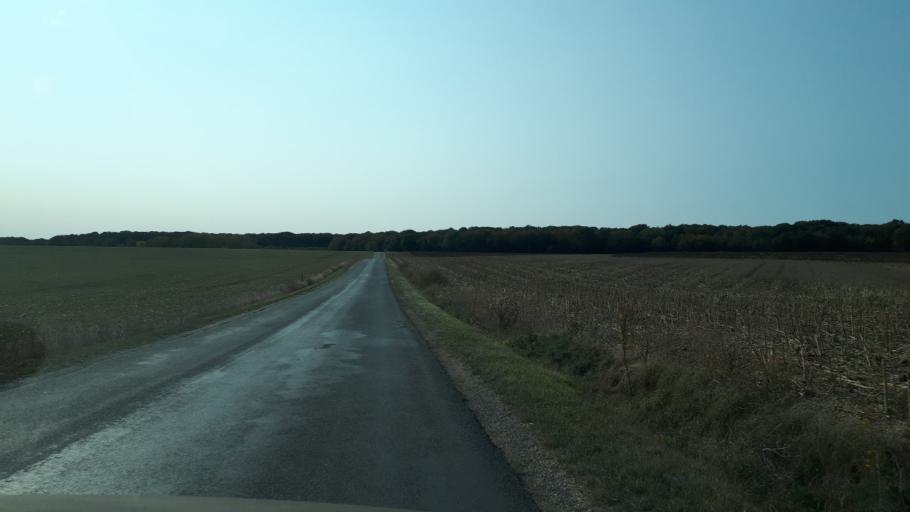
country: FR
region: Centre
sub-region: Departement du Cher
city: Rians
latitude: 47.1855
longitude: 2.6560
